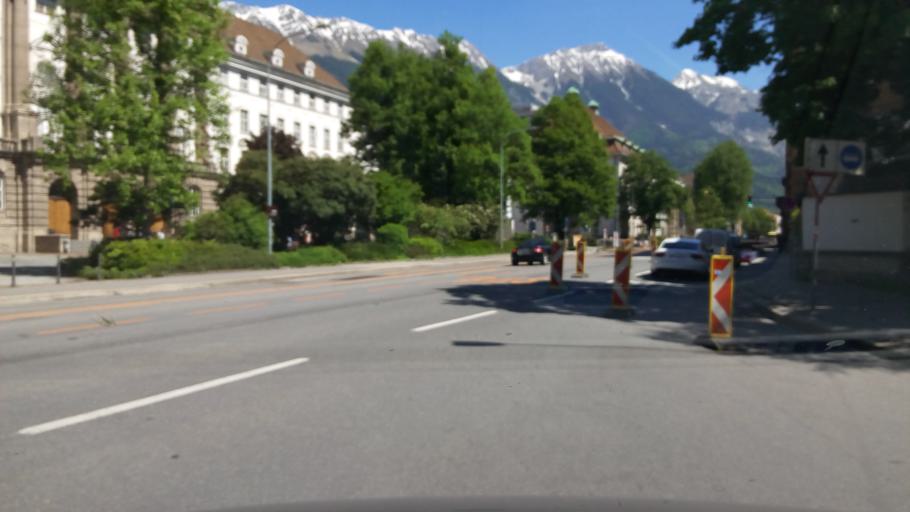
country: AT
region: Tyrol
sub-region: Innsbruck Stadt
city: Innsbruck
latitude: 47.2622
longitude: 11.3847
